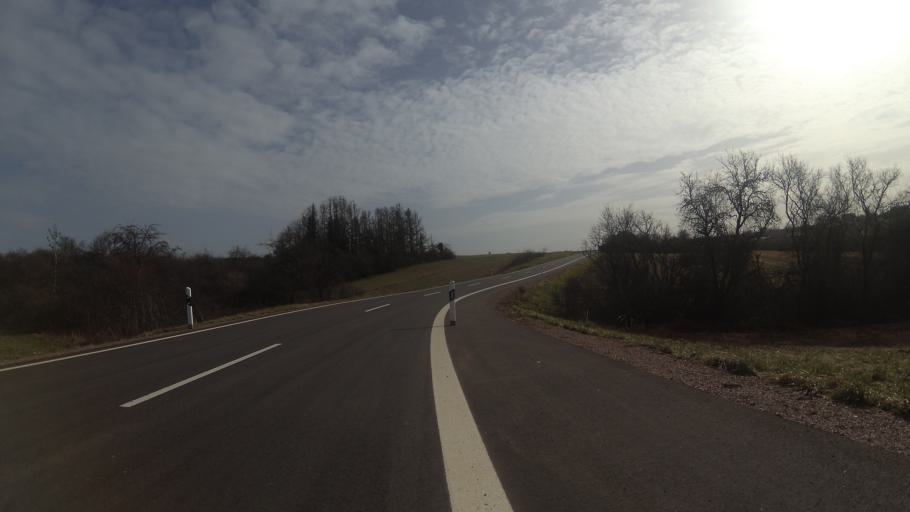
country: FR
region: Lorraine
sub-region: Departement de la Moselle
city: Merten
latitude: 49.3020
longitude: 6.6664
